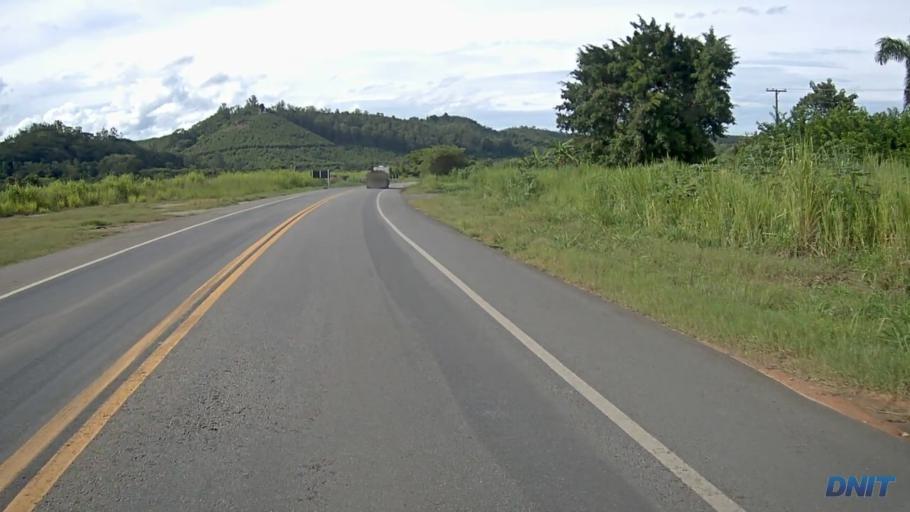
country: BR
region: Minas Gerais
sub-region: Belo Oriente
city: Belo Oriente
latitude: -19.2813
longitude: -42.3570
